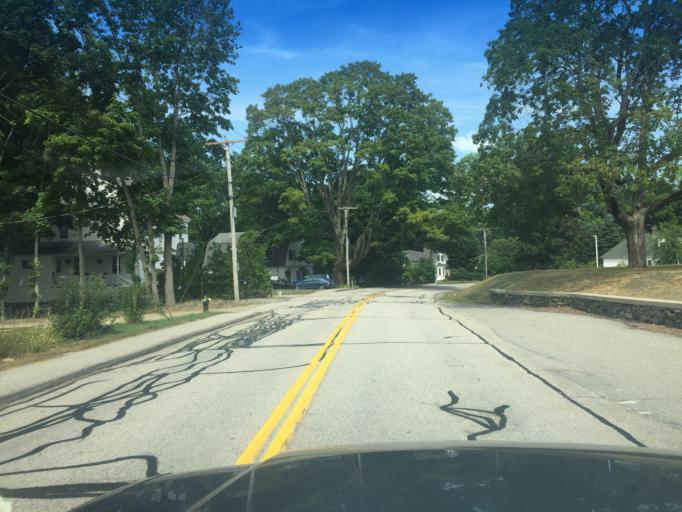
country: US
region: Maine
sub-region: York County
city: York Harbor
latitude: 43.1456
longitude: -70.6629
